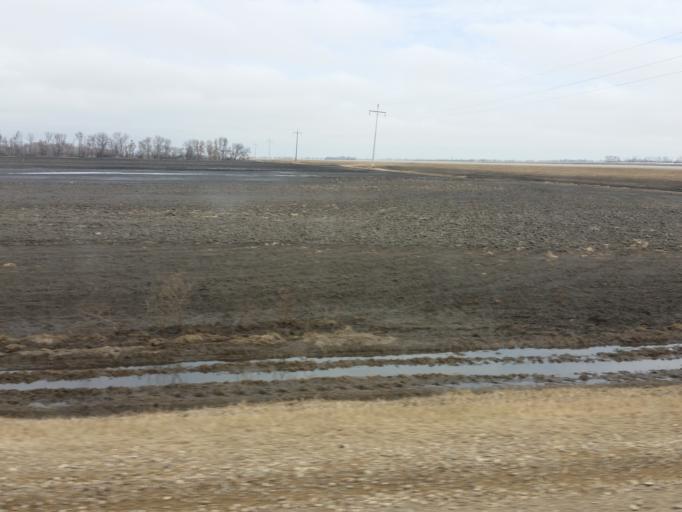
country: US
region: North Dakota
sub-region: Walsh County
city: Grafton
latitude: 48.4129
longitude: -97.3212
